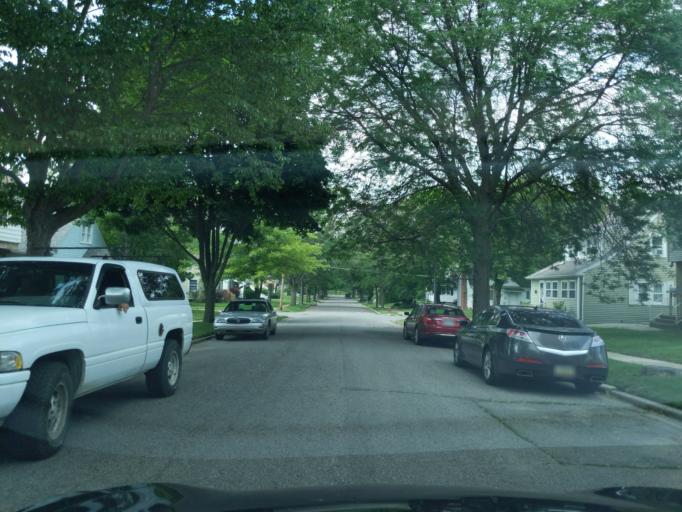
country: US
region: Michigan
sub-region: Ingham County
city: Lansing
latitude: 42.7168
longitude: -84.5714
